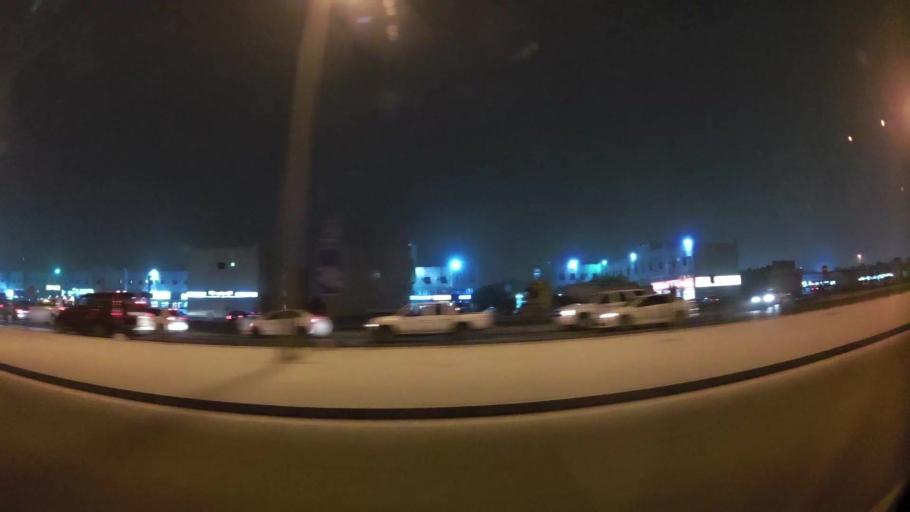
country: QA
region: Baladiyat ad Dawhah
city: Doha
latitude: 25.2459
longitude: 51.4740
